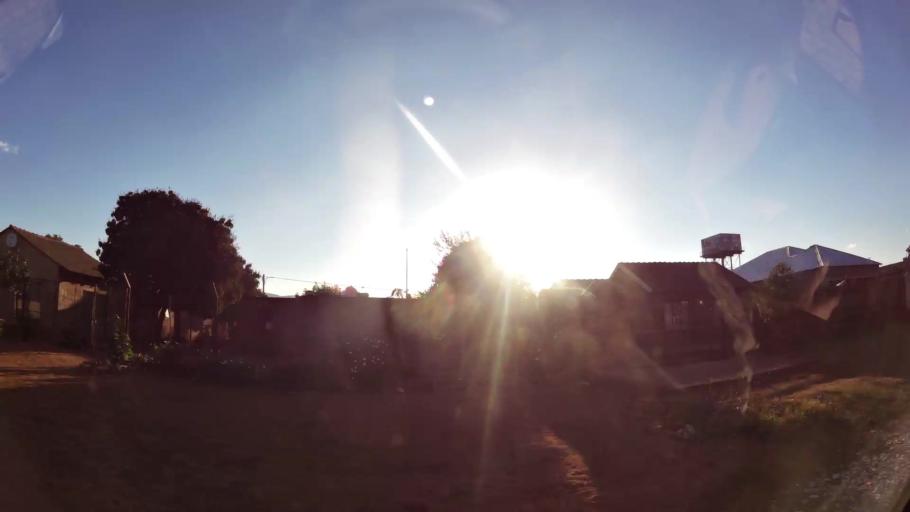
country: ZA
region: Limpopo
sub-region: Waterberg District Municipality
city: Mokopane
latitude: -24.1531
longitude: 28.9913
